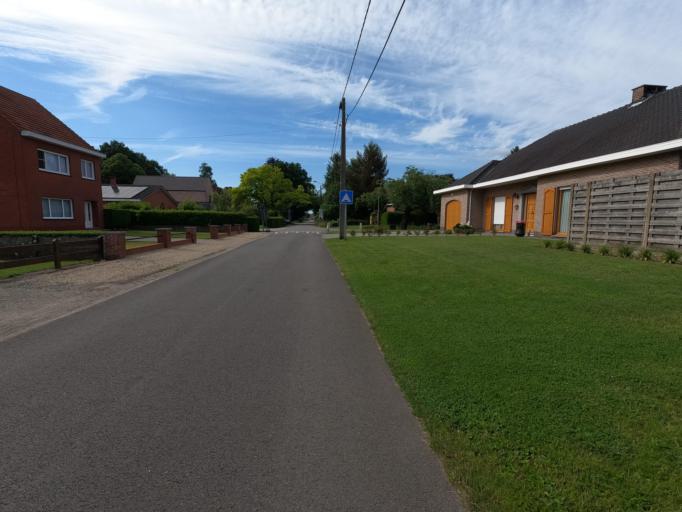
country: BE
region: Flanders
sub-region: Provincie Antwerpen
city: Zandhoven
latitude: 51.2595
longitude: 4.6521
